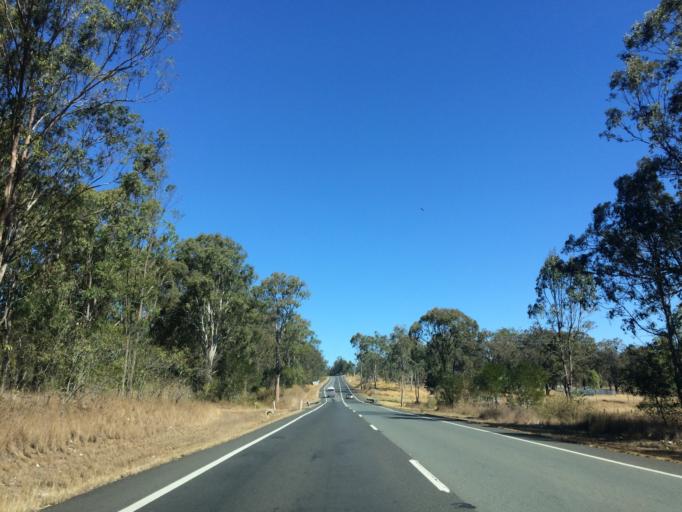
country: AU
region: Queensland
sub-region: Ipswich
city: Thagoona
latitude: -28.0079
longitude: 152.5253
